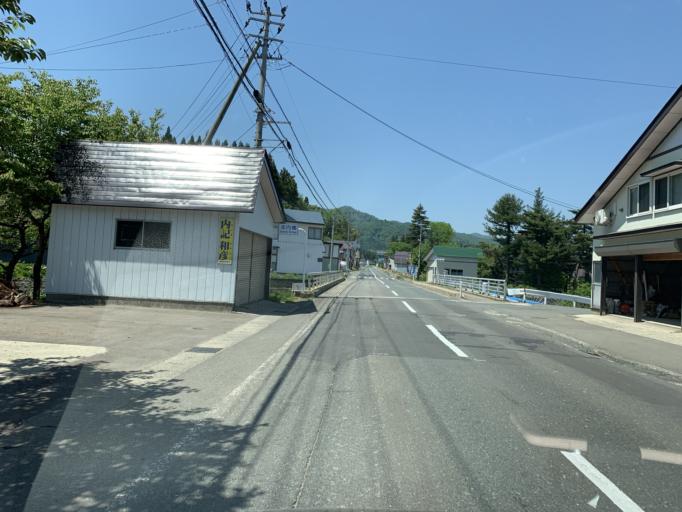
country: JP
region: Akita
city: Yokotemachi
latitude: 39.4068
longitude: 140.7522
